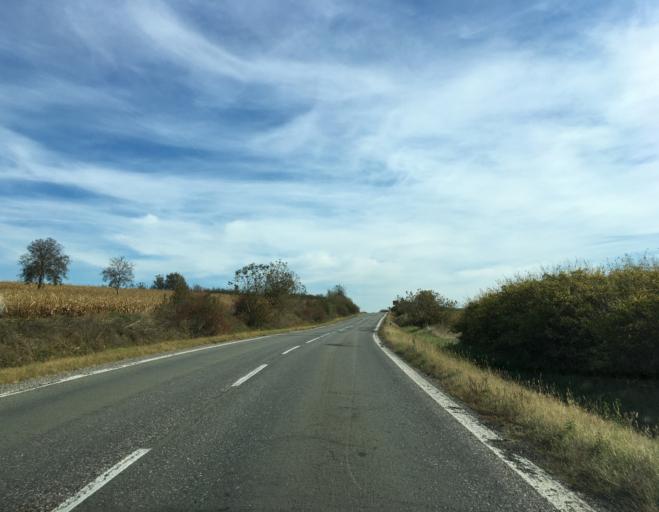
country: SK
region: Nitriansky
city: Svodin
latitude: 48.0339
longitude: 18.4550
